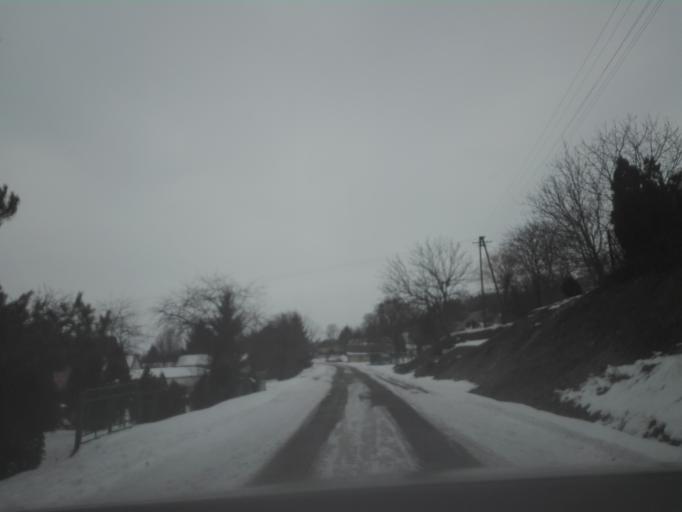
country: PL
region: Lublin Voivodeship
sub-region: Powiat hrubieszowski
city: Horodlo
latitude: 50.8456
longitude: 24.0285
